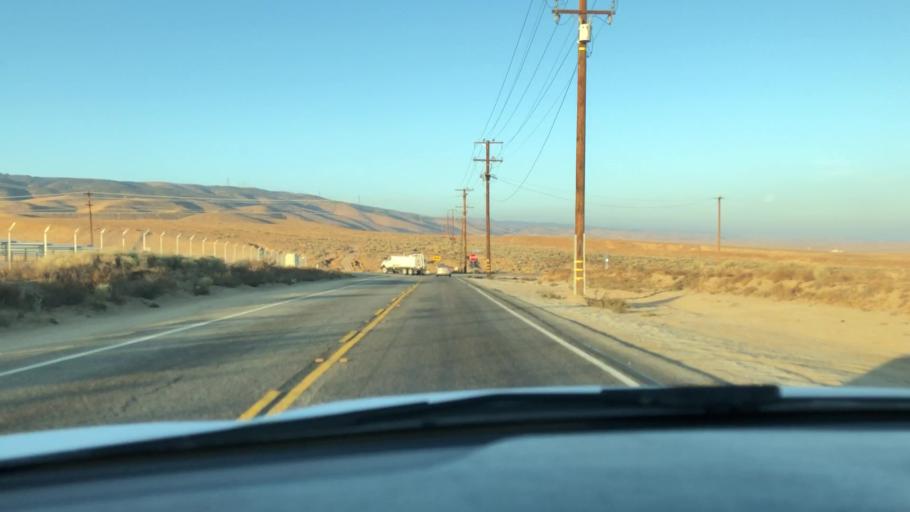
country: US
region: California
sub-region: Los Angeles County
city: Leona Valley
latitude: 34.6747
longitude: -118.3229
